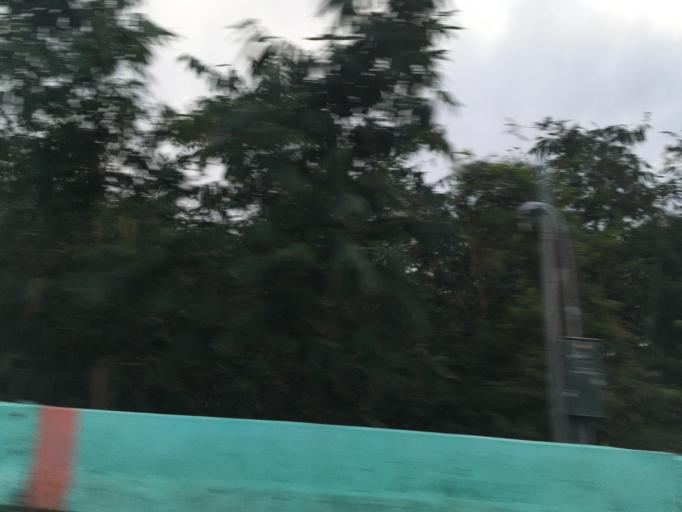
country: TW
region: Taiwan
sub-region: Yilan
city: Yilan
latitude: 24.7495
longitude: 121.7159
